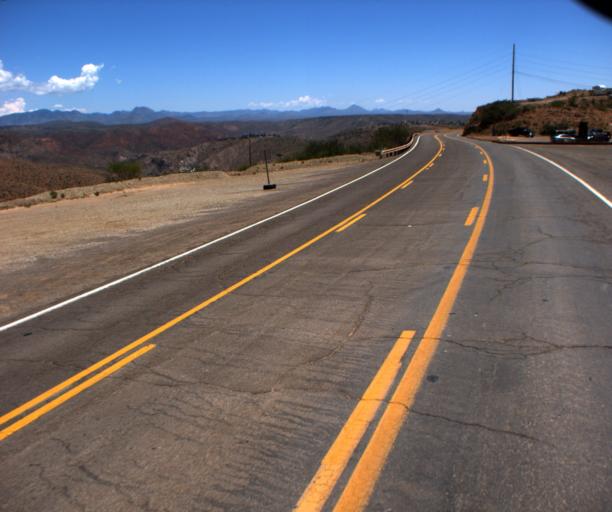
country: US
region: Arizona
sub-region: Greenlee County
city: Morenci
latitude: 33.0640
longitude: -109.3355
